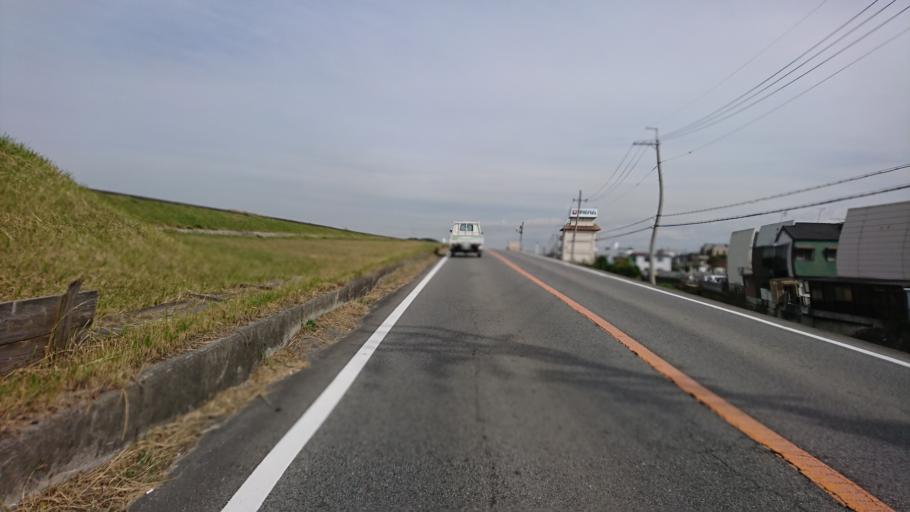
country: JP
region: Hyogo
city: Kakogawacho-honmachi
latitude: 34.7752
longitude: 134.8408
